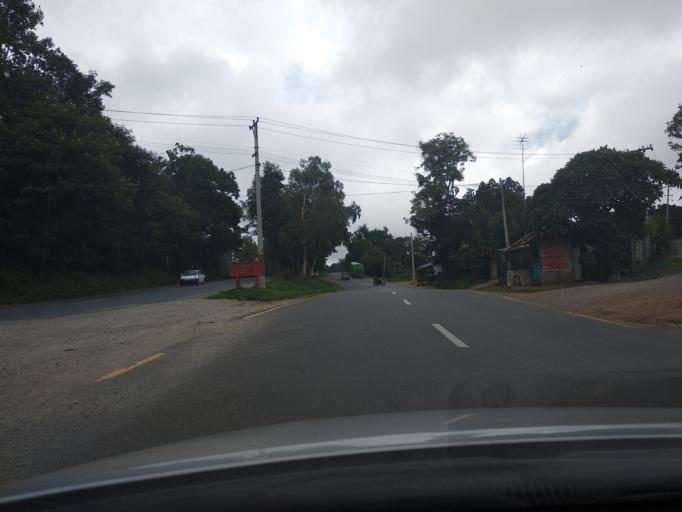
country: MM
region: Mandalay
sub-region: Pyin Oo Lwin District
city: Pyin Oo Lwin
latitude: 21.9242
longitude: 96.3759
